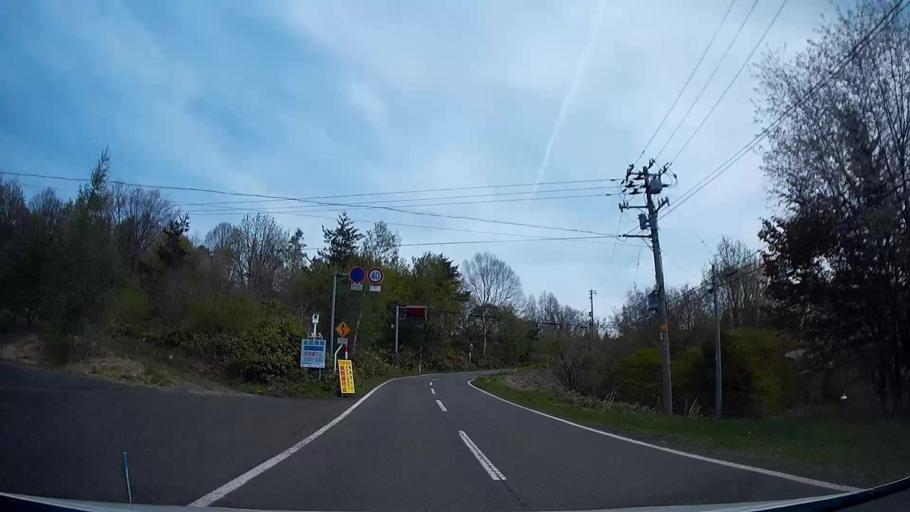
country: JP
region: Iwate
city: Shizukuishi
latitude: 39.9221
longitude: 140.9758
